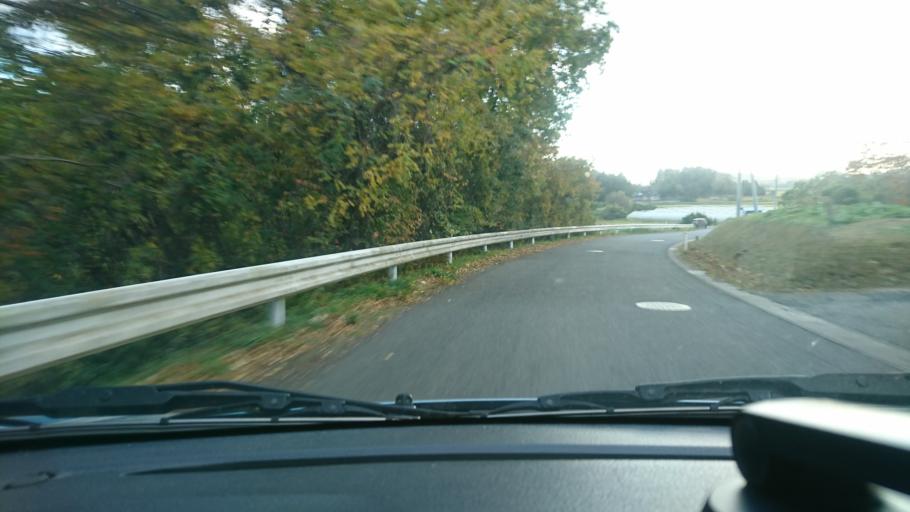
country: JP
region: Iwate
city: Ichinoseki
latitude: 38.7800
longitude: 141.2165
